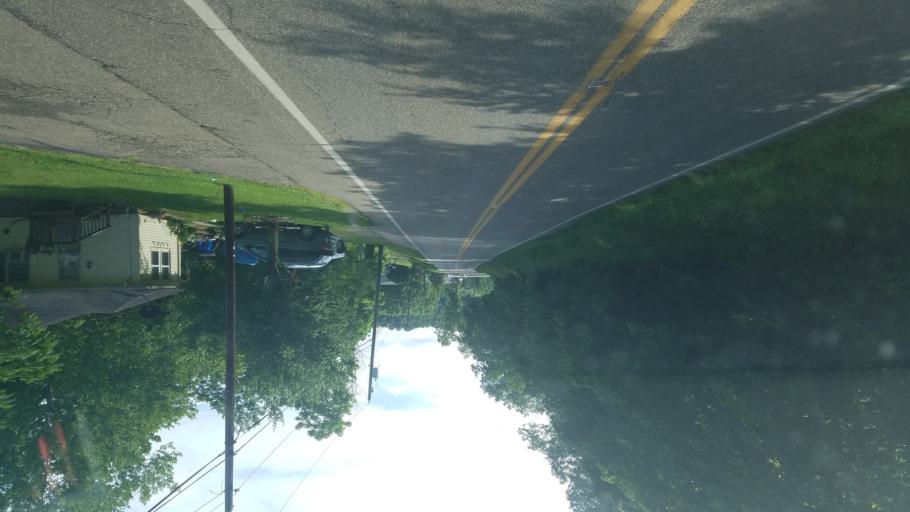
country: US
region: Ohio
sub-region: Gallia County
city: Gallipolis
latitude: 38.8163
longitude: -82.2278
